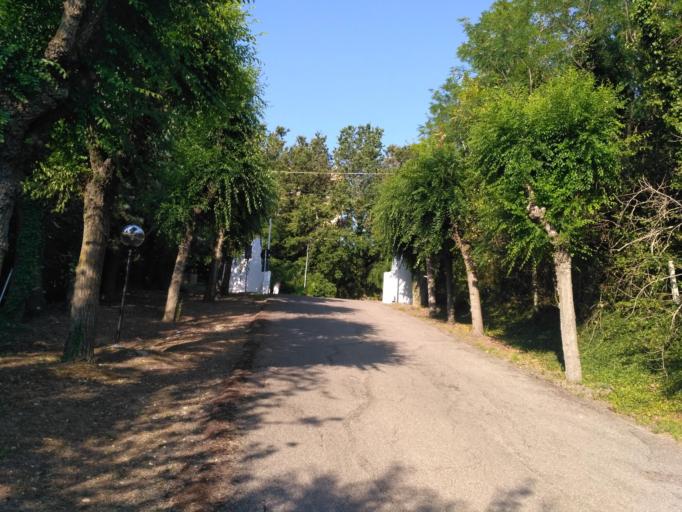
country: IT
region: The Marches
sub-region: Provincia di Pesaro e Urbino
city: Gradara
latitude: 43.9613
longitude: 12.7836
